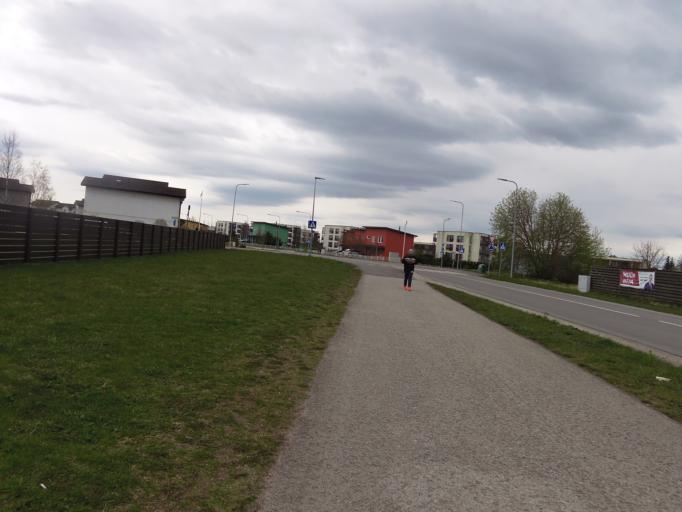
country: EE
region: Harju
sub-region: Tallinna linn
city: Tallinn
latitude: 59.3924
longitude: 24.8086
